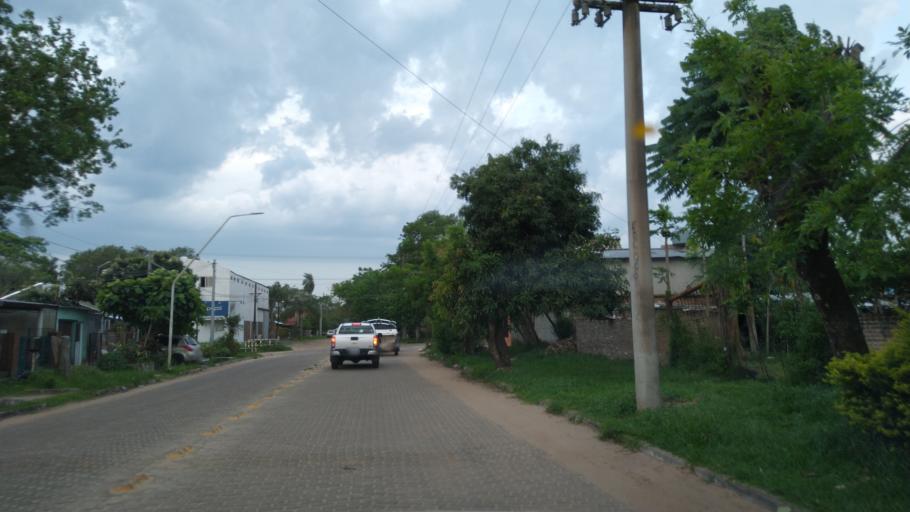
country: AR
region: Corrientes
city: Ituzaingo
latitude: -27.5883
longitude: -56.6972
